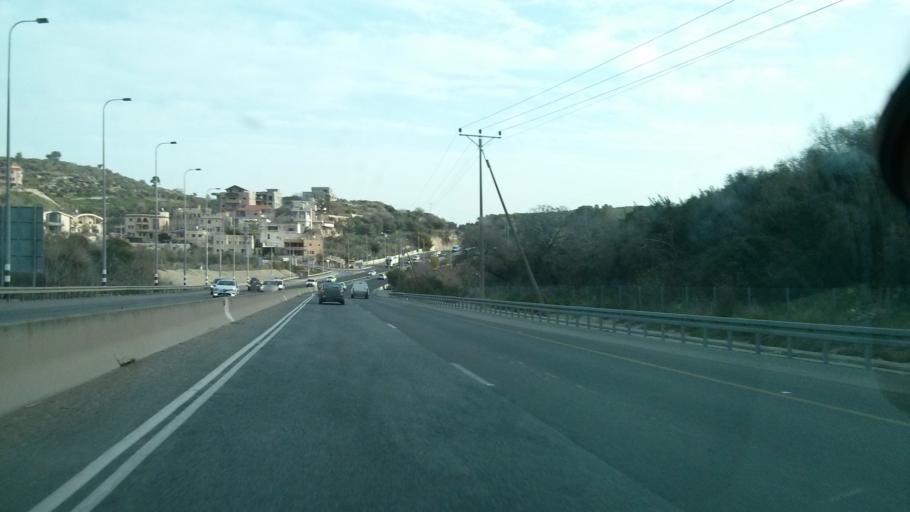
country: IL
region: Haifa
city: Umm el Fahm
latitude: 32.5527
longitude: 35.1657
